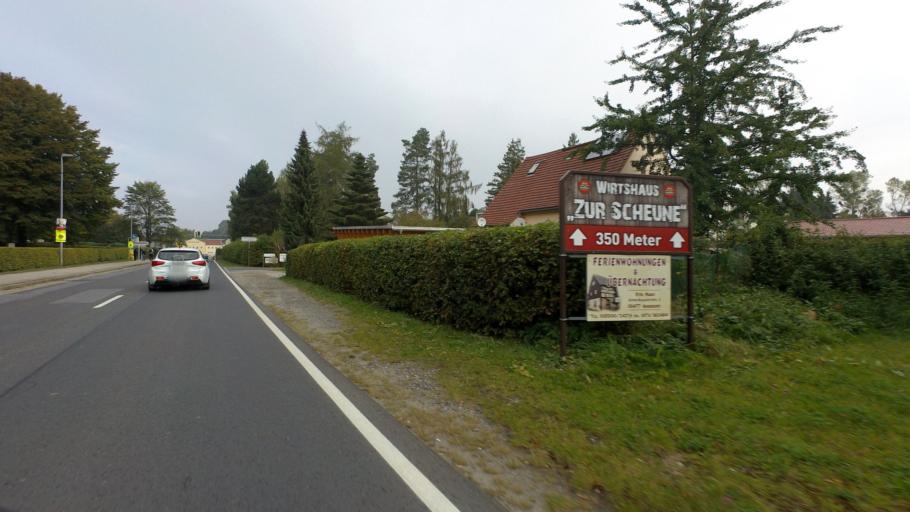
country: DE
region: Saxony
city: Arnsdorf
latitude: 51.0963
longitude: 13.9964
